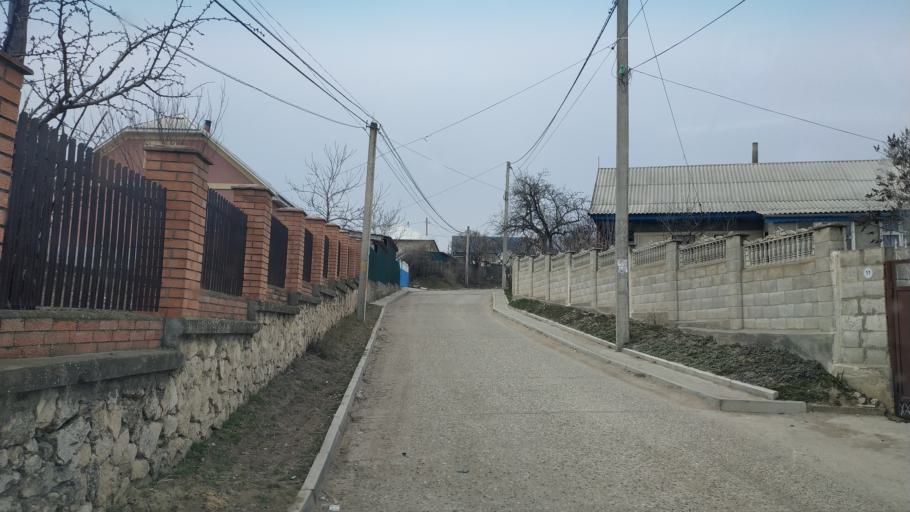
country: MD
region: Chisinau
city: Singera
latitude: 46.8240
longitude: 29.0328
